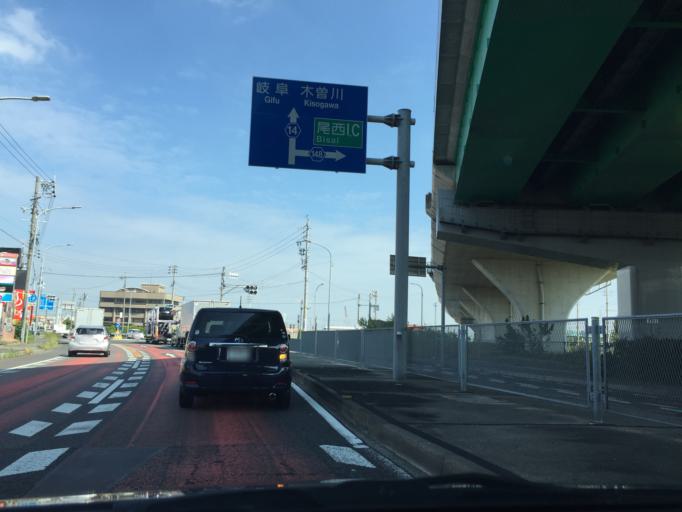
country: JP
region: Aichi
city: Ichinomiya
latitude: 35.3071
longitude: 136.7737
